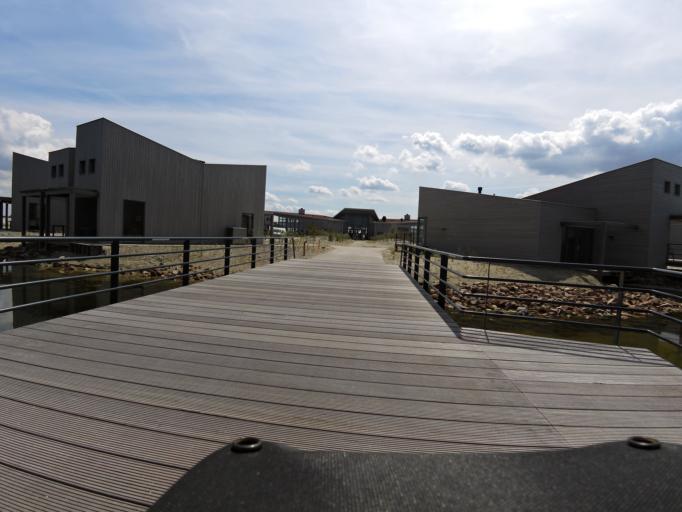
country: NL
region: South Holland
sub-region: Gemeente Goeree-Overflakkee
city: Ouddorp
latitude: 51.7810
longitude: 3.8842
